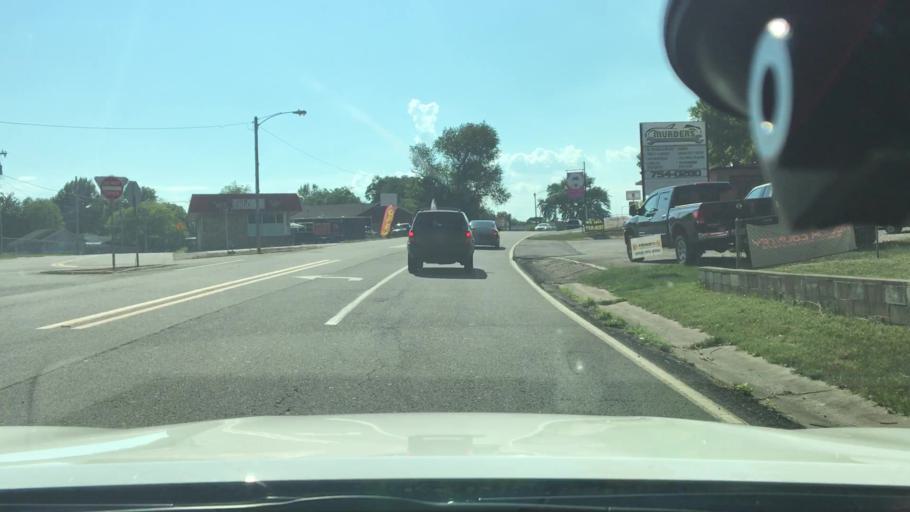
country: US
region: Arkansas
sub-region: Johnson County
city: Clarksville
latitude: 35.4716
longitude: -93.4807
